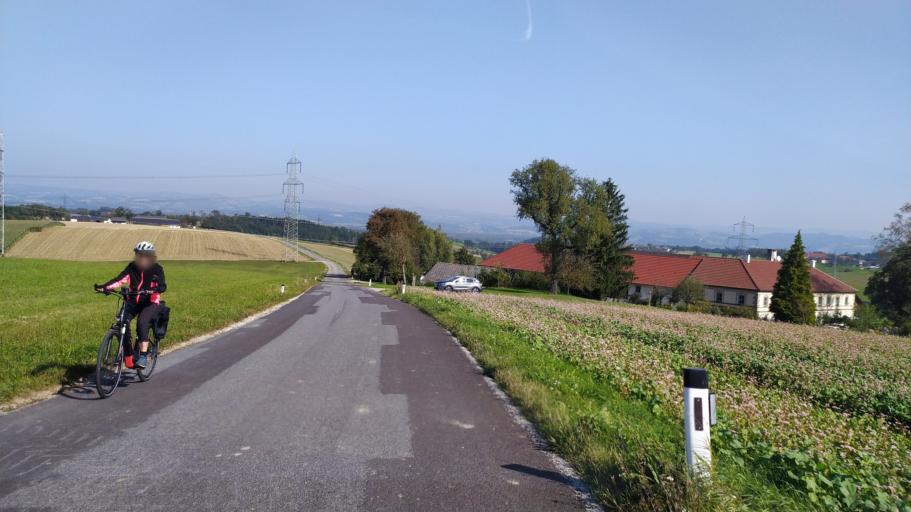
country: AT
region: Lower Austria
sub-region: Politischer Bezirk Amstetten
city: Zeillern
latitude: 48.1306
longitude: 14.7536
